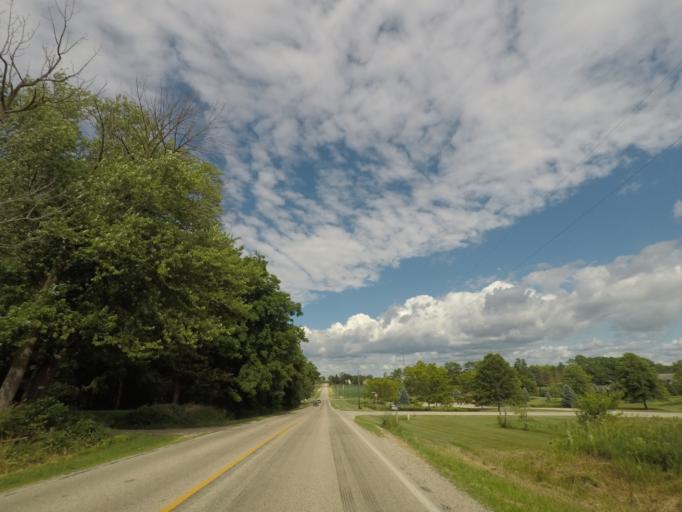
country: US
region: Wisconsin
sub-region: Rock County
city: Janesville
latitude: 42.7012
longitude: -89.1046
